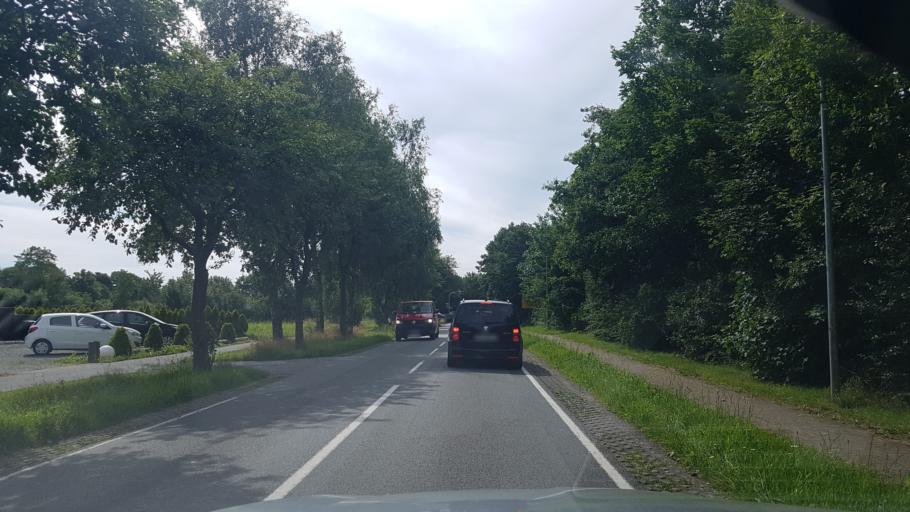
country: DE
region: Schleswig-Holstein
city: Handewitt
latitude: 54.7792
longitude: 9.3286
